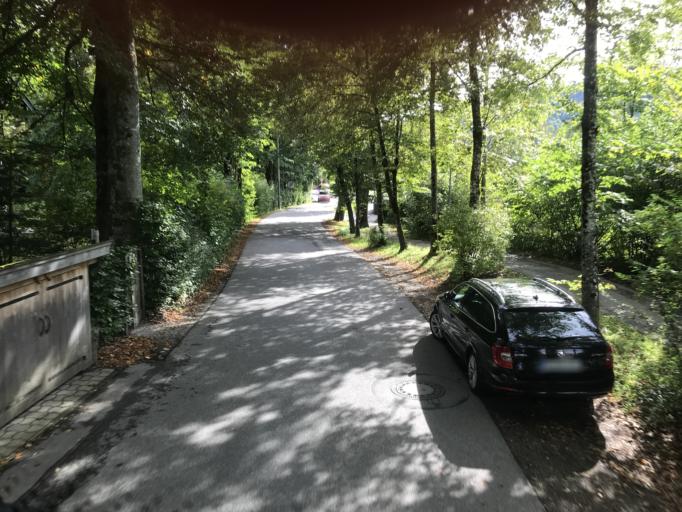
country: DE
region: Bavaria
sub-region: Upper Bavaria
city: Rottach-Egern
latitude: 47.6882
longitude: 11.7600
